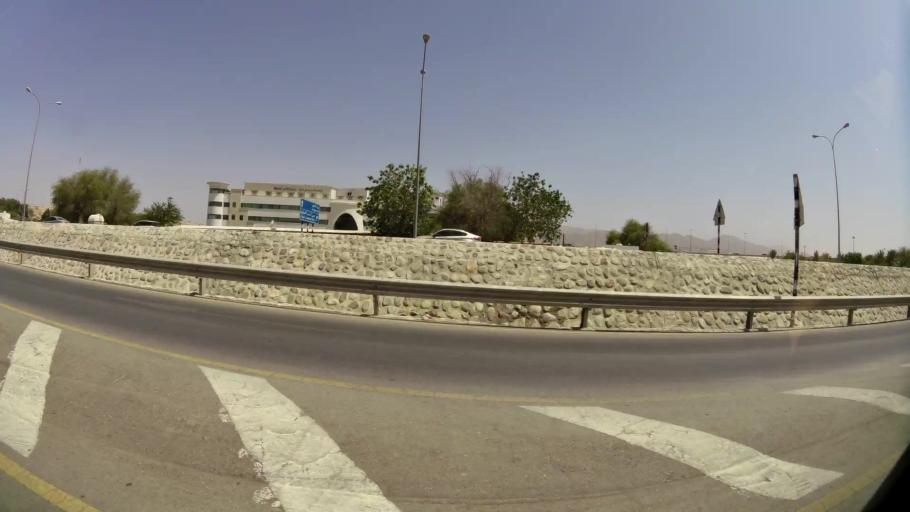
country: OM
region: Muhafazat Masqat
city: Muscat
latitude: 23.6183
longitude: 58.4973
